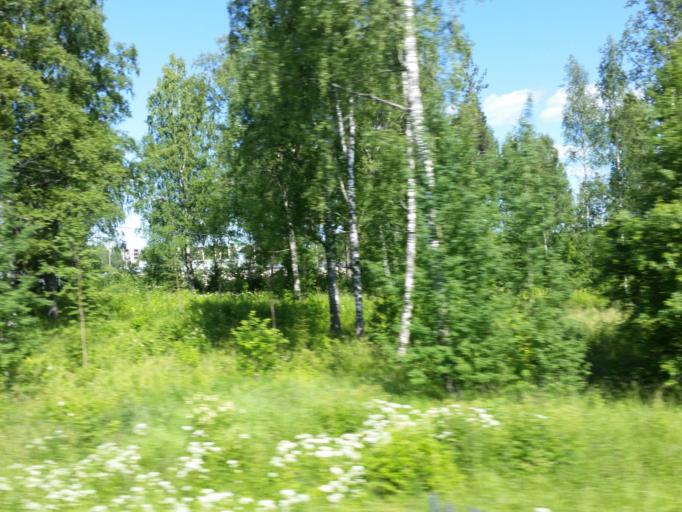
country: FI
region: Northern Savo
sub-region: Varkaus
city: Varkaus
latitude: 62.3071
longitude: 27.8586
